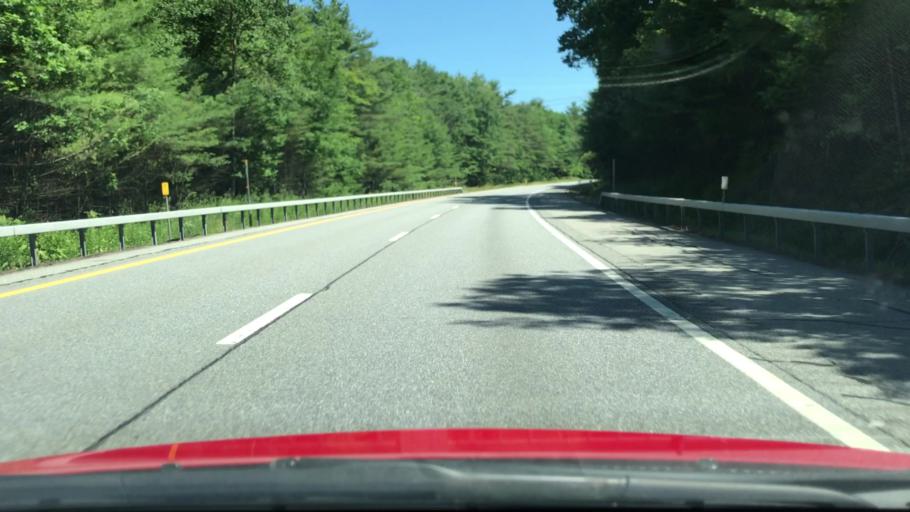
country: US
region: New York
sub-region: Warren County
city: Warrensburg
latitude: 43.5118
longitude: -73.7435
